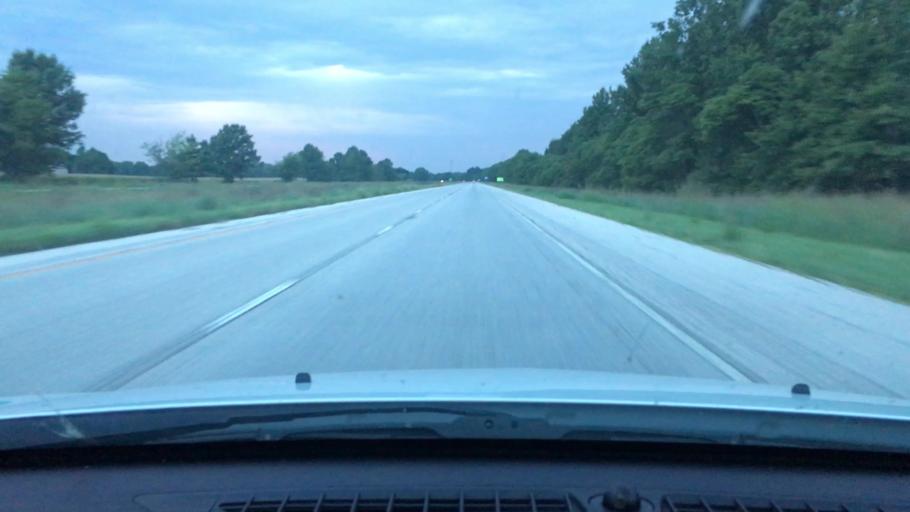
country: US
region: Illinois
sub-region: Morgan County
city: Jacksonville
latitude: 39.7380
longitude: -90.1335
